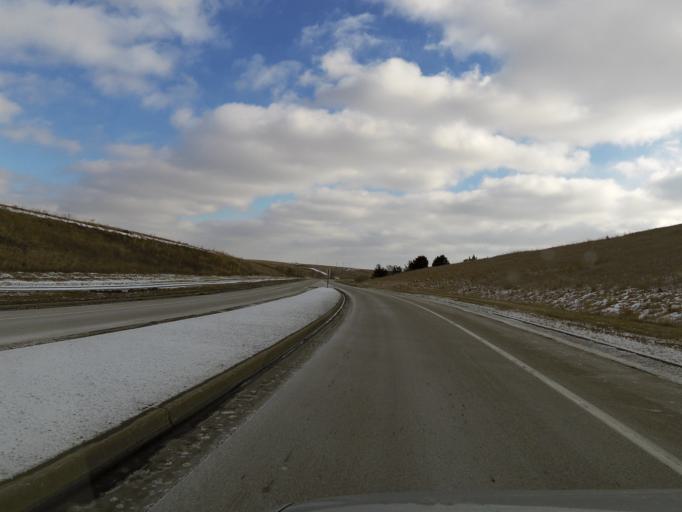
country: US
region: Minnesota
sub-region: Hennepin County
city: Eden Prairie
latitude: 44.8328
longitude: -93.4796
